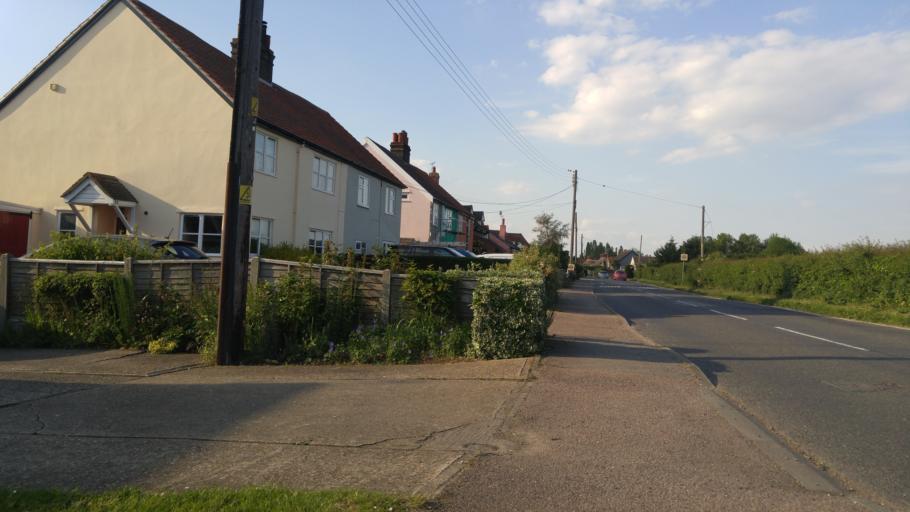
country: GB
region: England
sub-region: Essex
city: Eight Ash Green
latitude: 51.9204
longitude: 0.8025
